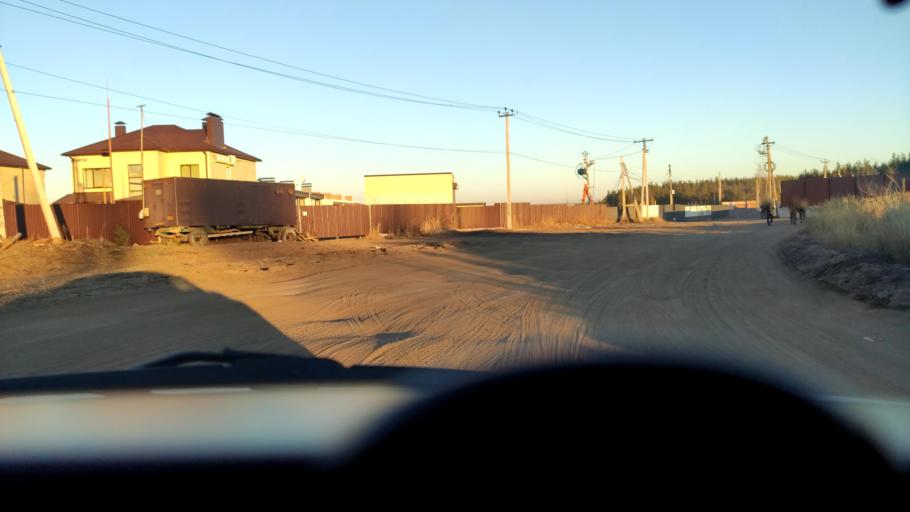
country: RU
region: Voronezj
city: Podgornoye
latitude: 51.7470
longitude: 39.1415
